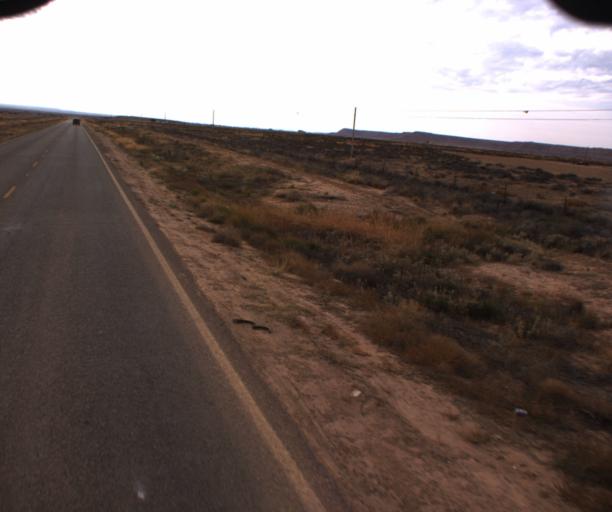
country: US
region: Arizona
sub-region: Apache County
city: Many Farms
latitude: 36.3248
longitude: -109.6187
